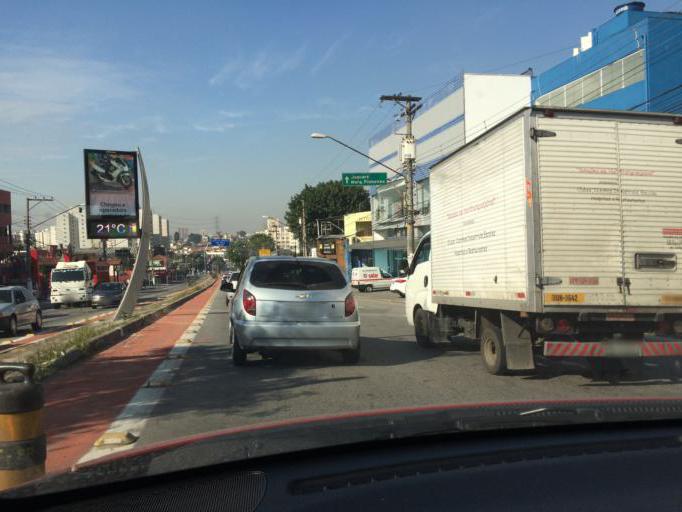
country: BR
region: Sao Paulo
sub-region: Osasco
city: Osasco
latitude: -23.5501
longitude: -46.7582
